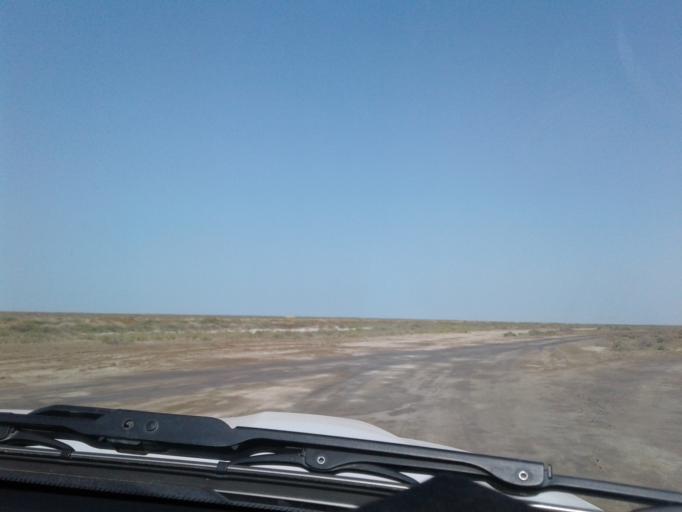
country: IR
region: Golestan
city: Gomishan
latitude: 37.8436
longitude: 53.8855
